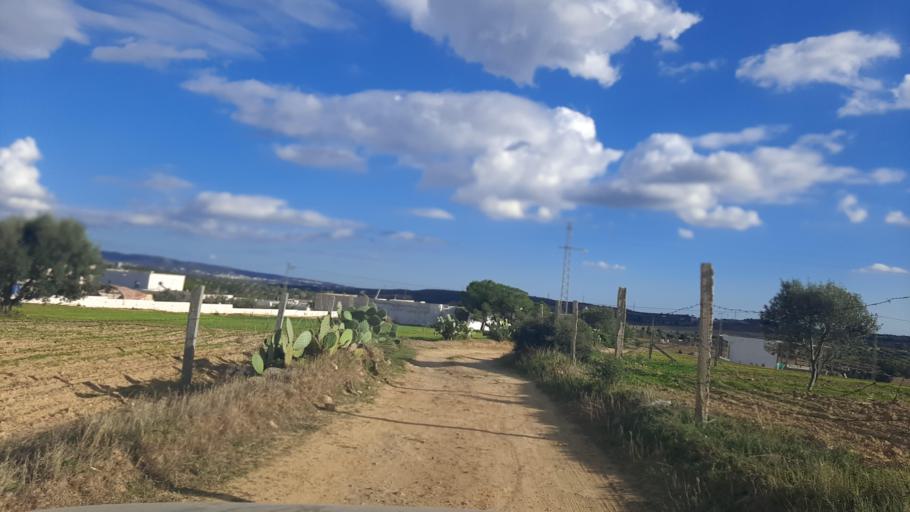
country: TN
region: Nabul
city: Bu `Urqub
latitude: 36.4564
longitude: 10.4968
